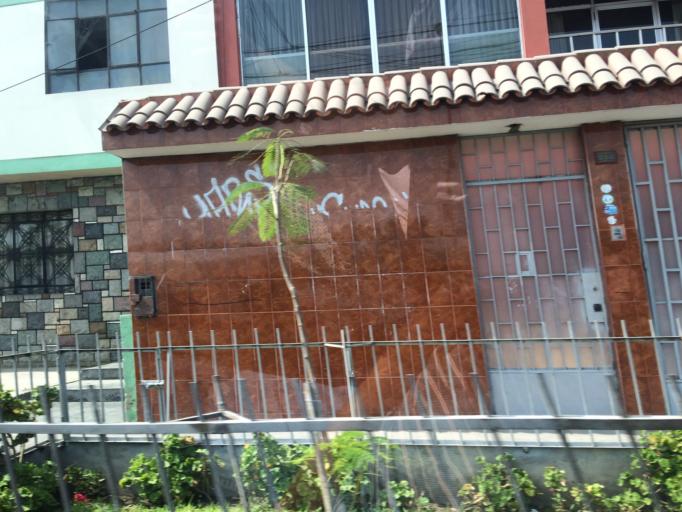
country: PE
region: Lima
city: Lima
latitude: -12.0261
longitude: -77.0392
